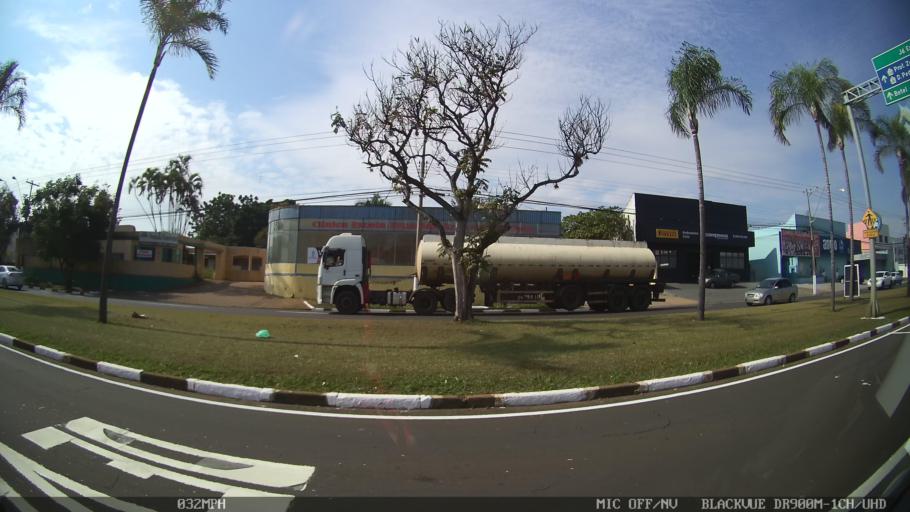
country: BR
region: Sao Paulo
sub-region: Paulinia
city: Paulinia
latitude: -22.7767
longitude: -47.1446
